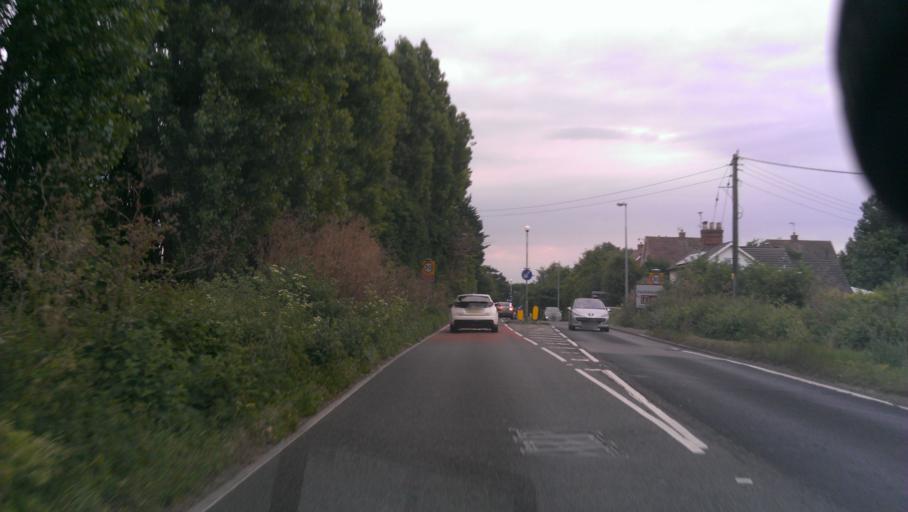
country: GB
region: England
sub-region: Kent
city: Faversham
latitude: 51.3054
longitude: 0.9055
